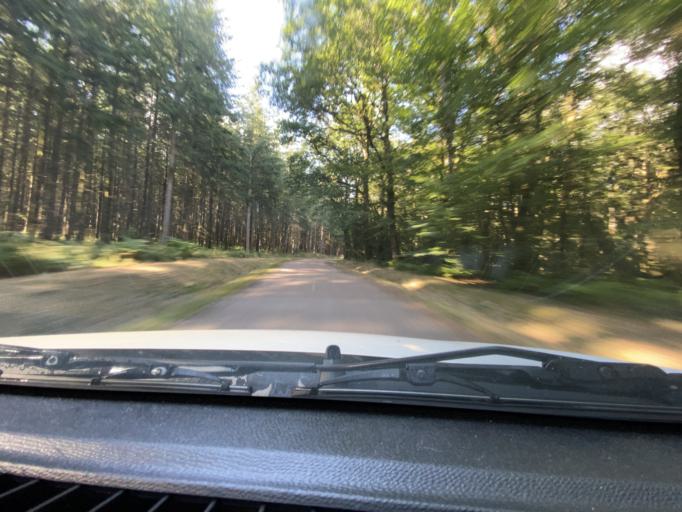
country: FR
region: Bourgogne
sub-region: Departement de la Cote-d'Or
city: Saulieu
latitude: 47.2944
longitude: 4.1714
